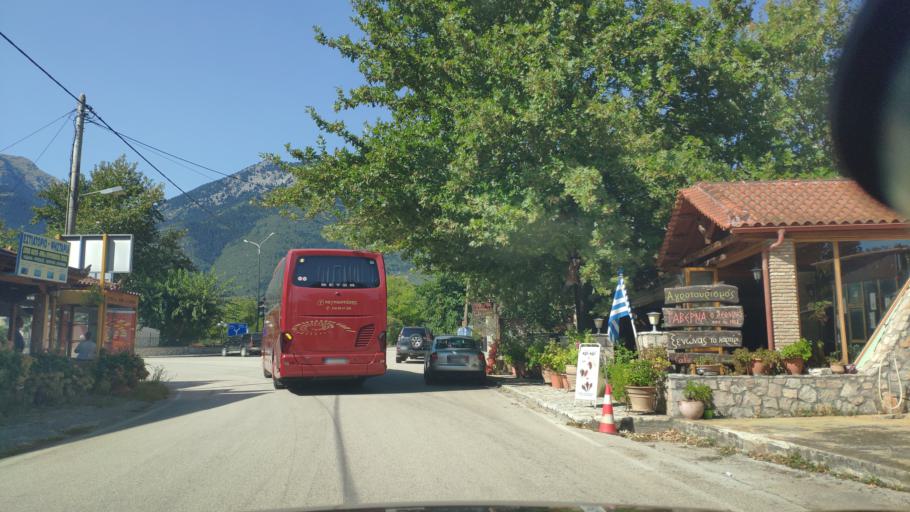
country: GR
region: Peloponnese
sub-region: Nomos Korinthias
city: Nemea
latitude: 37.8449
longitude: 22.4079
